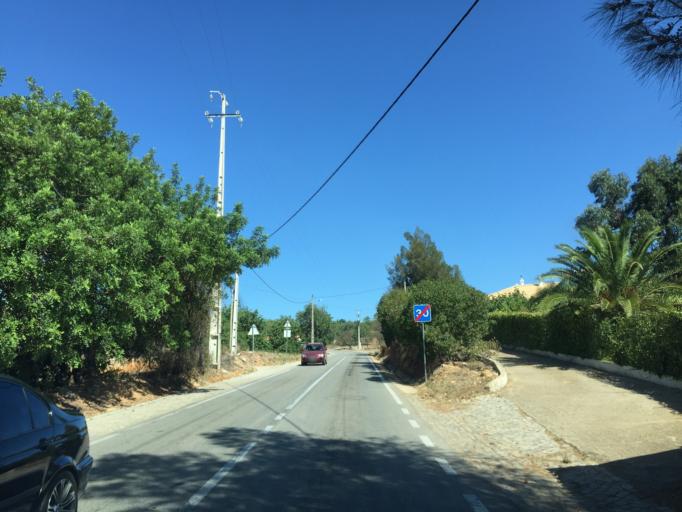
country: PT
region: Faro
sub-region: Loule
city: Vilamoura
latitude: 37.1142
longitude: -8.0913
